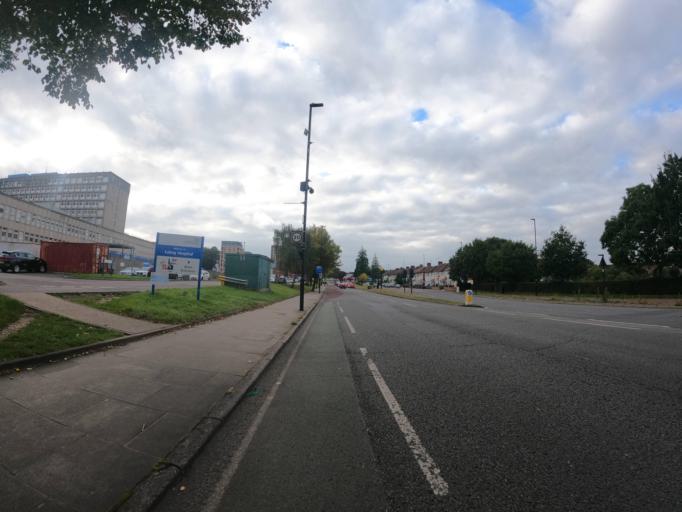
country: GB
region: England
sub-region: Greater London
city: Greenford
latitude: 51.5084
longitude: -0.3440
